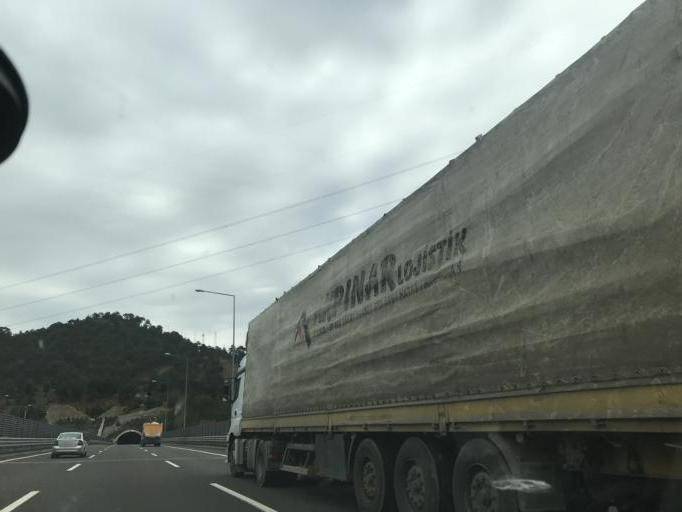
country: TR
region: Nigde
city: Ciftehan
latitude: 37.5055
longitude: 34.8213
